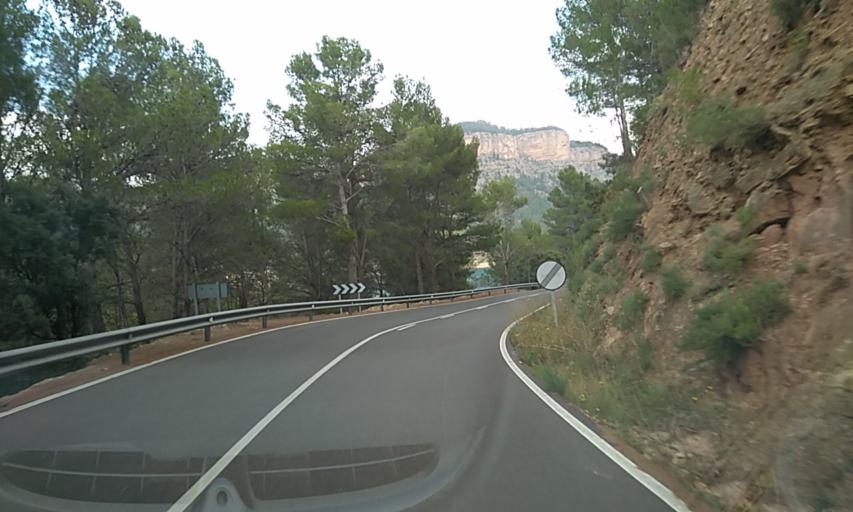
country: ES
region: Valencia
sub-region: Provincia de Castello
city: Puebla de Arenoso
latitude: 40.0948
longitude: -0.5728
